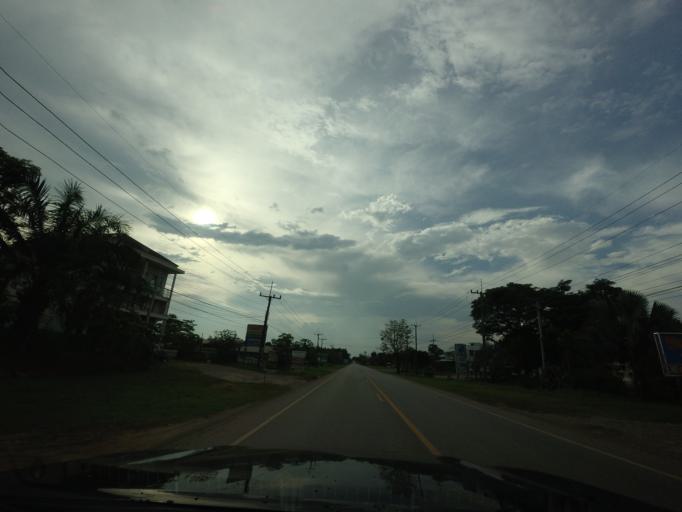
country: TH
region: Changwat Udon Thani
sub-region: Amphoe Ban Phue
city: Ban Phue
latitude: 17.6996
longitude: 102.4449
